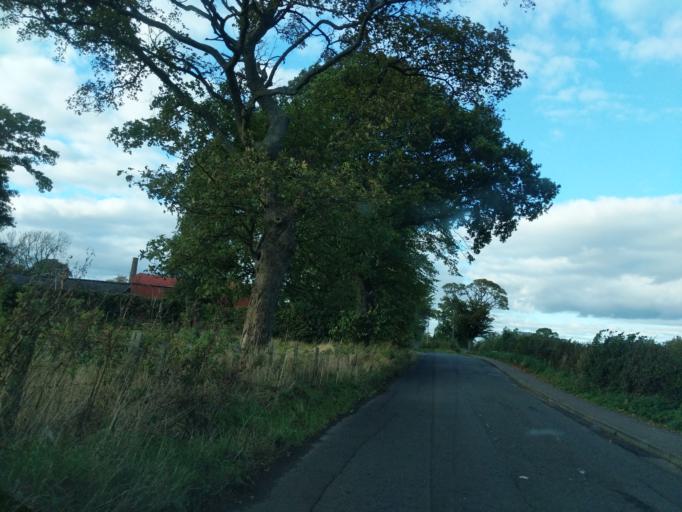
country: GB
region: Scotland
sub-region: Edinburgh
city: Queensferry
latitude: 55.9877
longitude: -3.3770
